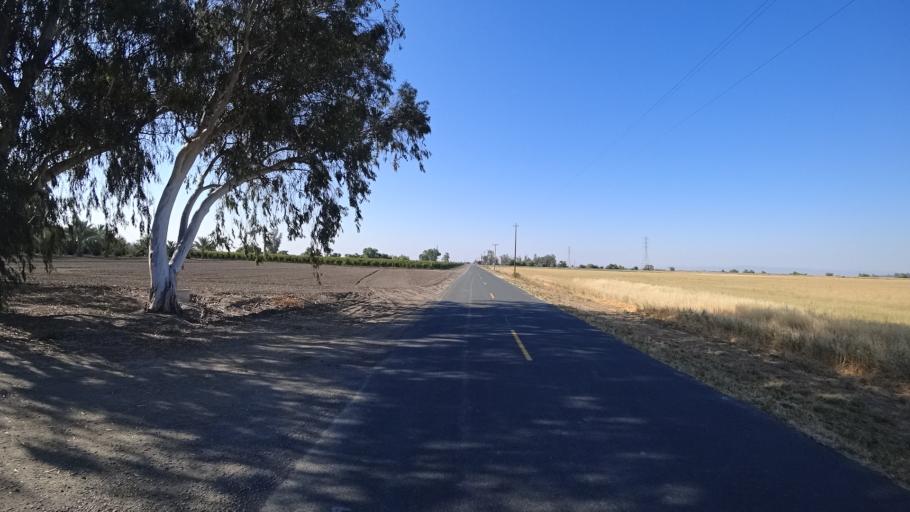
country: US
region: California
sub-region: Kings County
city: Lemoore Station
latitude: 36.3401
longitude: -119.8871
